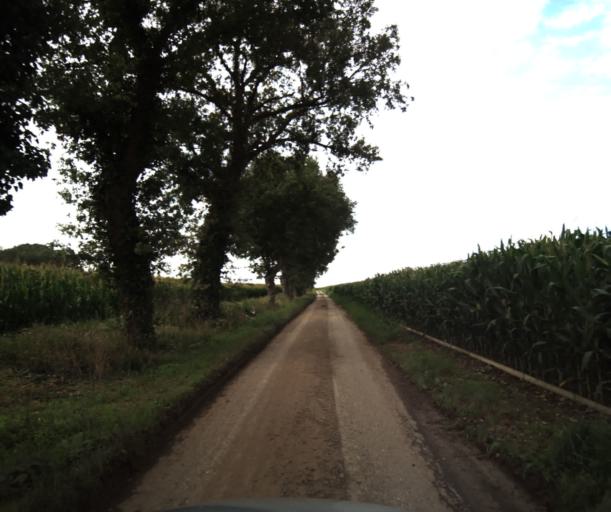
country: FR
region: Midi-Pyrenees
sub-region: Departement de la Haute-Garonne
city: Longages
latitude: 43.3871
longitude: 1.2361
